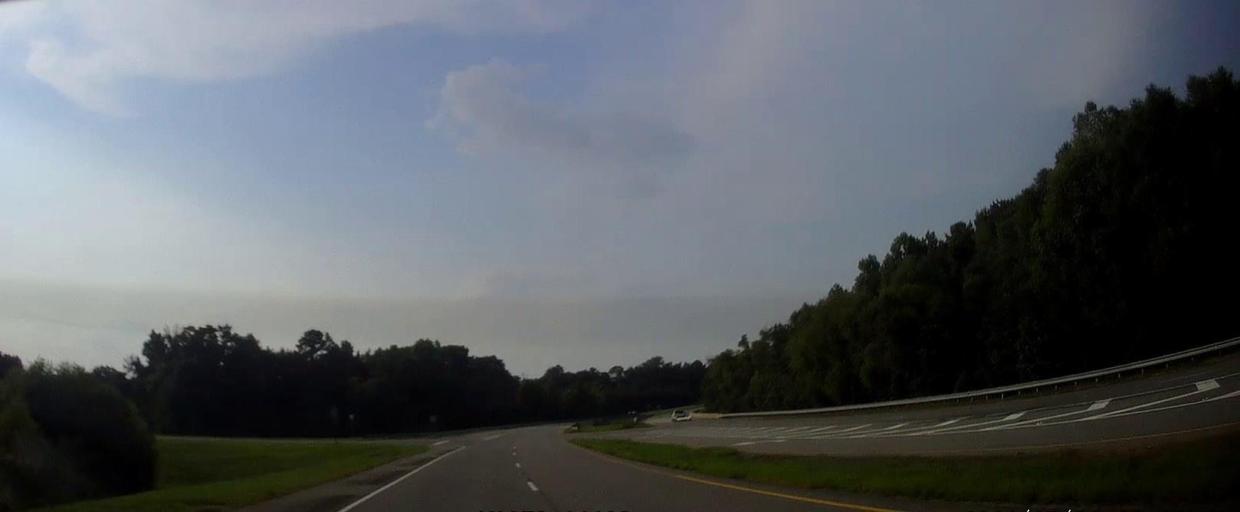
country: US
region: Georgia
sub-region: Laurens County
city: Dublin
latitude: 32.5450
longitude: -82.9779
